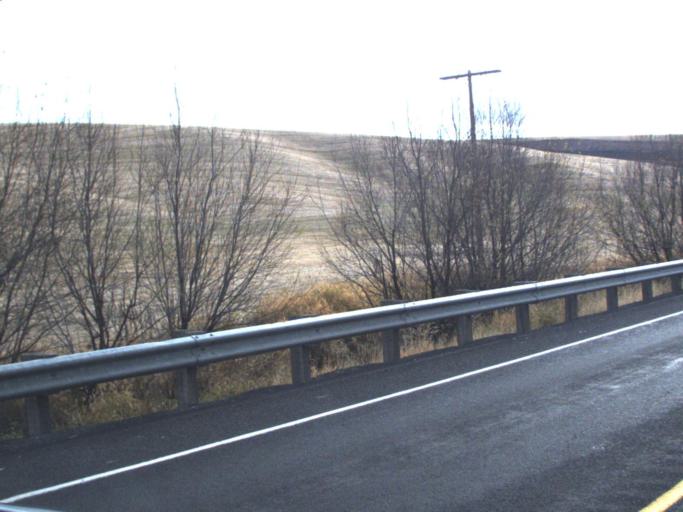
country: US
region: Washington
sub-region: Whitman County
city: Colfax
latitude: 46.8367
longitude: -117.4947
